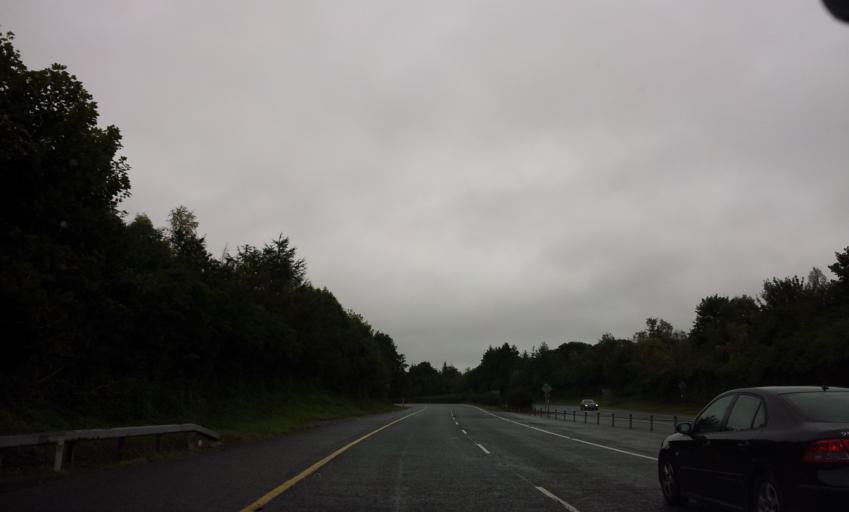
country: IE
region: Munster
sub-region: County Cork
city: Passage West
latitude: 51.9077
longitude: -8.3849
